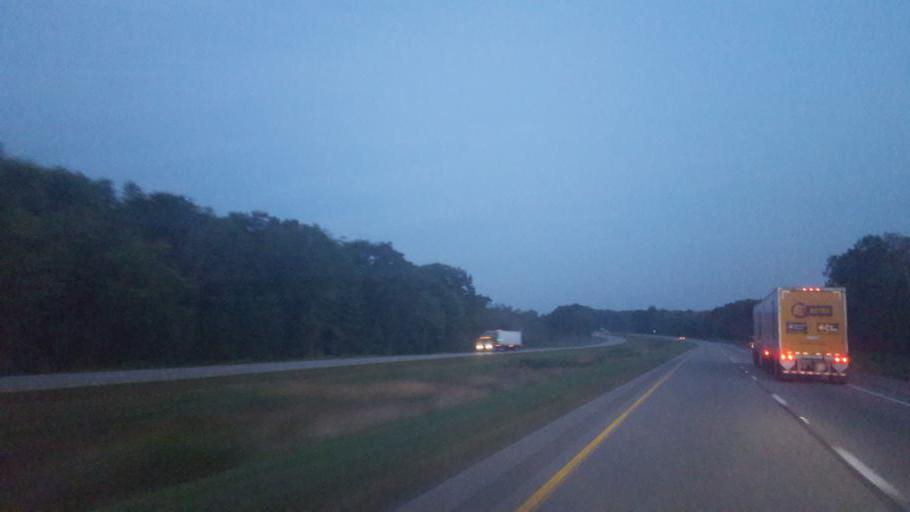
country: US
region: Pennsylvania
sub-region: Mercer County
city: Grove City
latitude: 41.2020
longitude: -79.9813
